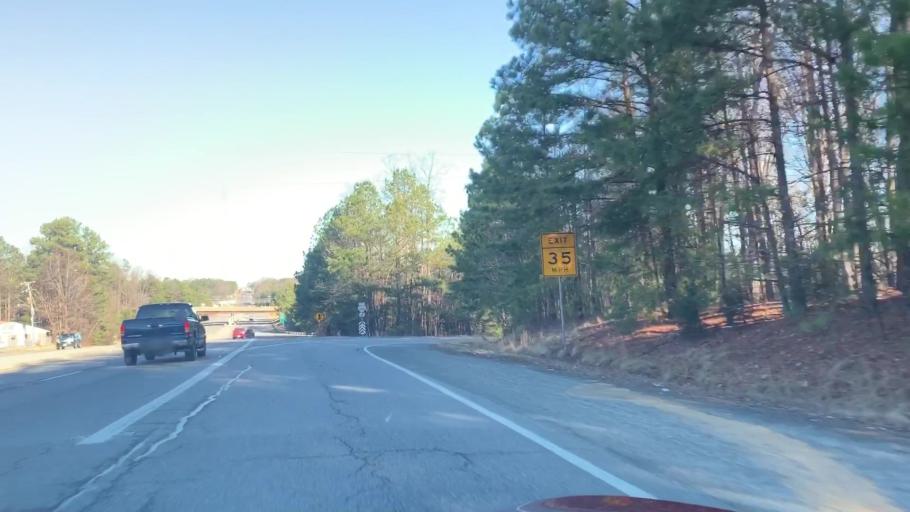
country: US
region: Virginia
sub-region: Chesterfield County
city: Chester
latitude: 37.3737
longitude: -77.4187
